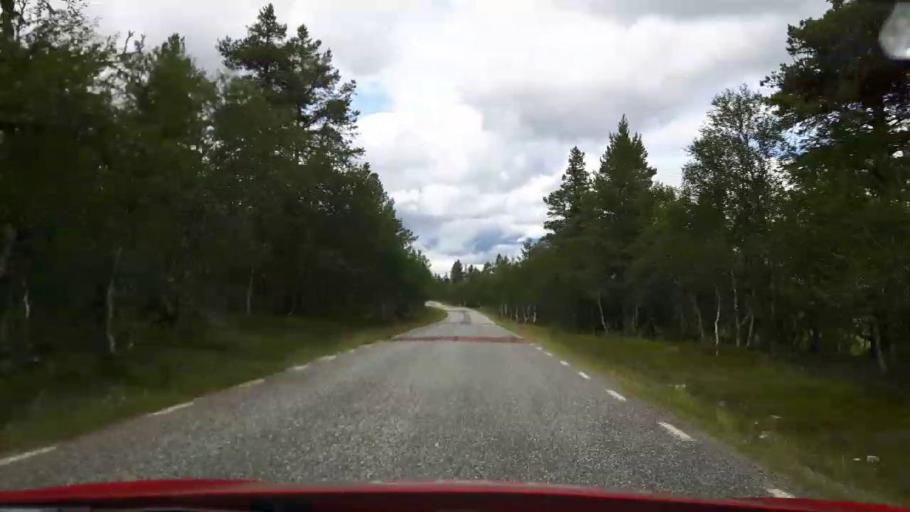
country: NO
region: Hedmark
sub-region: Trysil
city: Innbygda
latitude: 62.1206
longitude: 12.9713
